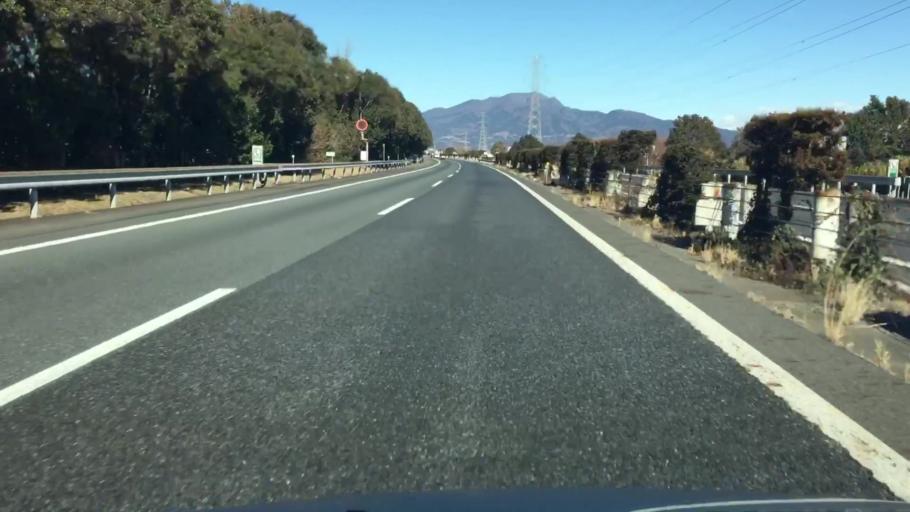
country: JP
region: Gunma
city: Shibukawa
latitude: 36.4518
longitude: 139.0145
